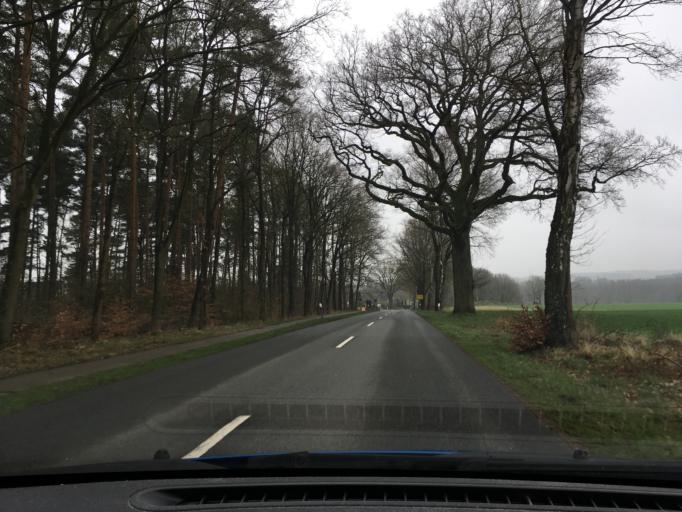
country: DE
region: Lower Saxony
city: Thomasburg
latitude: 53.2233
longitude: 10.6540
